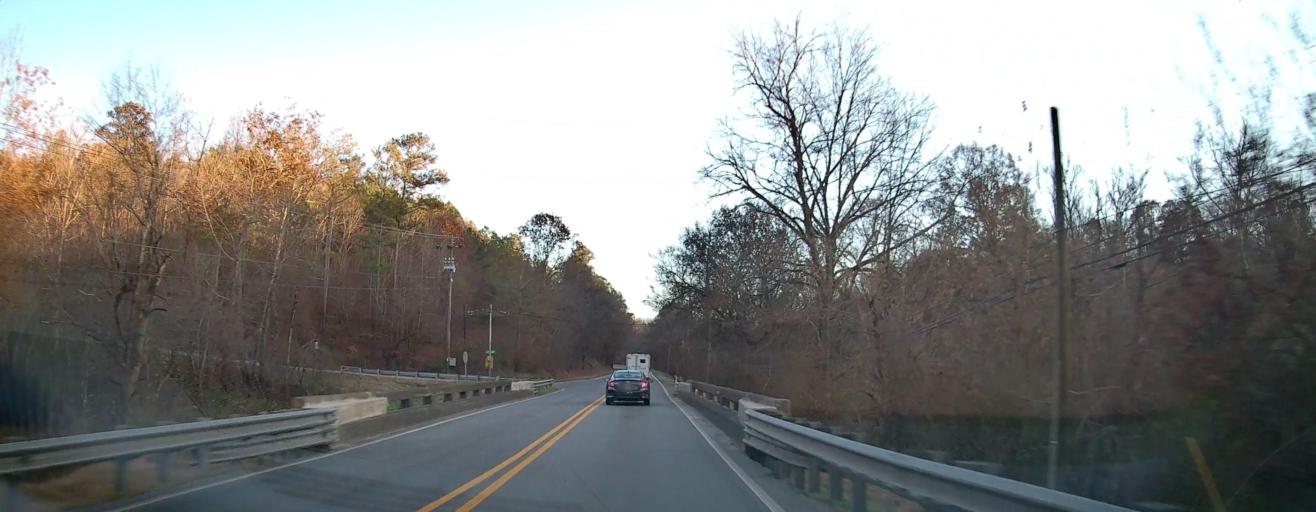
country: US
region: Alabama
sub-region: Etowah County
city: Attalla
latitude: 34.0450
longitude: -86.1560
